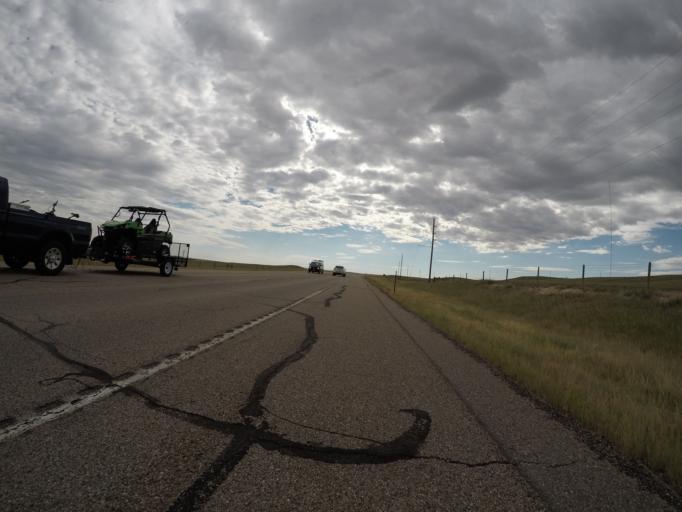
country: US
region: Wyoming
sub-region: Laramie County
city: Cheyenne
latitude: 41.1520
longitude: -104.9608
